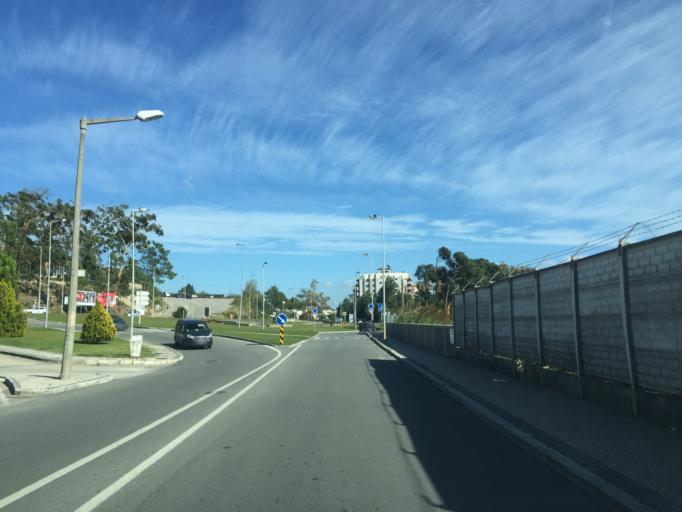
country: PT
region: Coimbra
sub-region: Figueira da Foz
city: Figueira da Foz
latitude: 40.1638
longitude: -8.8595
